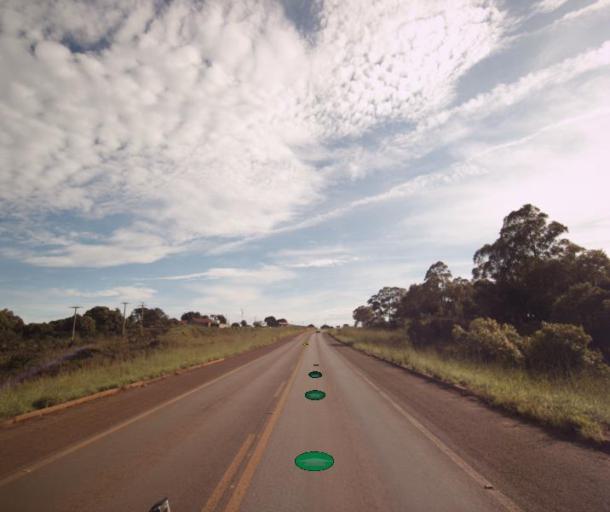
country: BR
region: Federal District
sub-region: Brasilia
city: Brasilia
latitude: -15.7421
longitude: -48.4101
